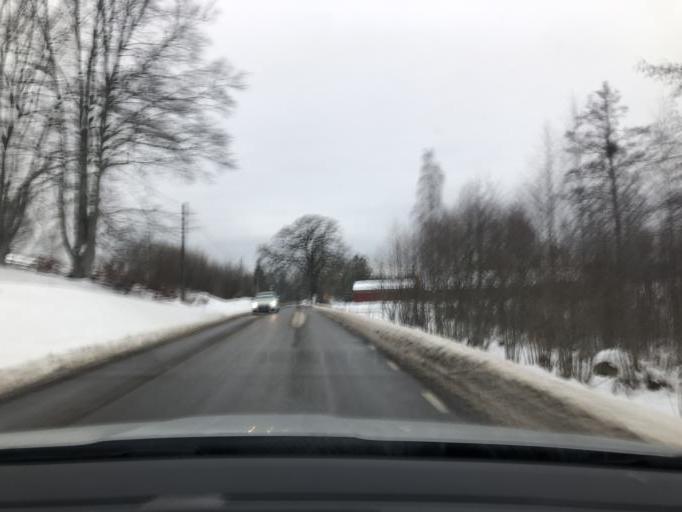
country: SE
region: OEstergoetland
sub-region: Kinda Kommun
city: Kisa
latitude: 57.9918
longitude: 15.6719
